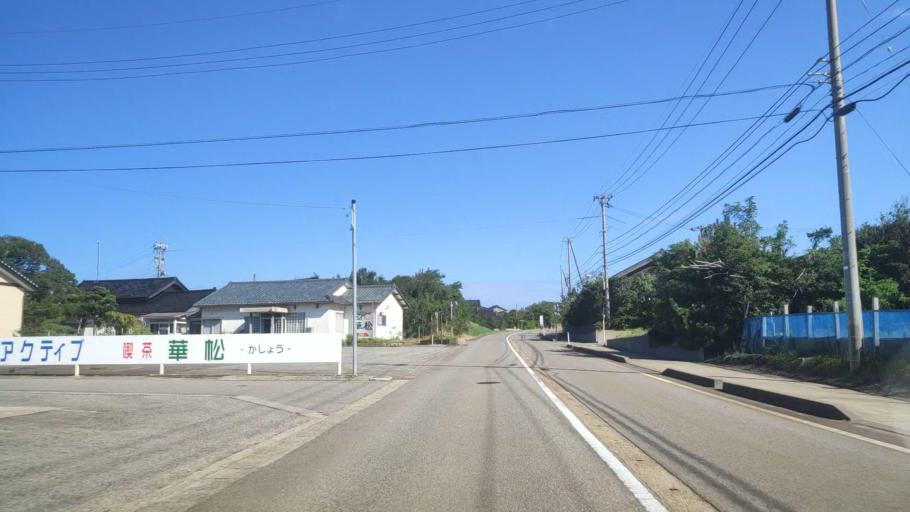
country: JP
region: Ishikawa
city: Hakui
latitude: 36.9845
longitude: 136.7758
